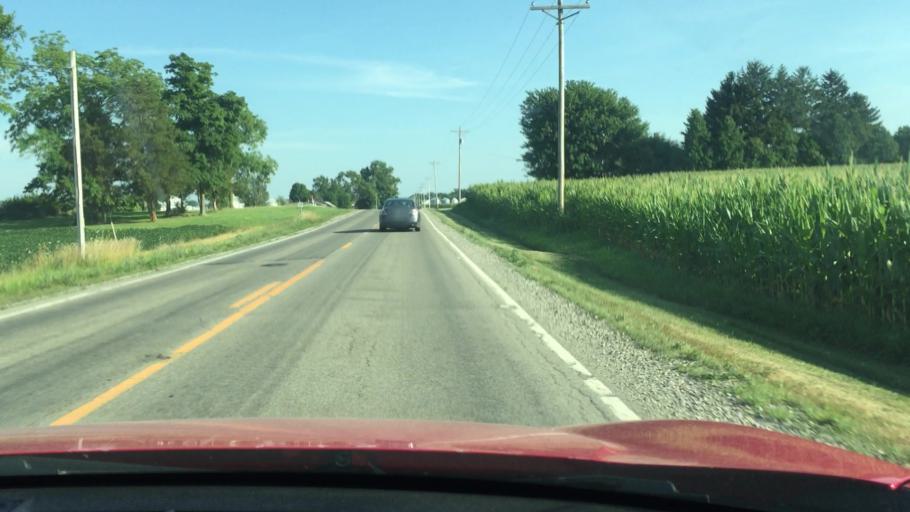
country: US
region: Ohio
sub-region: Hardin County
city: Ada
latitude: 40.6671
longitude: -83.8537
